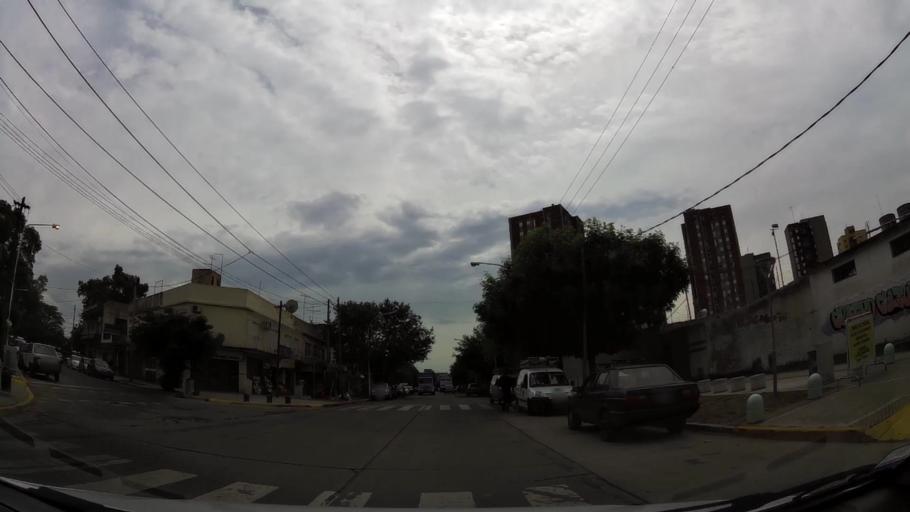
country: AR
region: Buenos Aires F.D.
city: Villa Lugano
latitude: -34.6852
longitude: -58.4926
